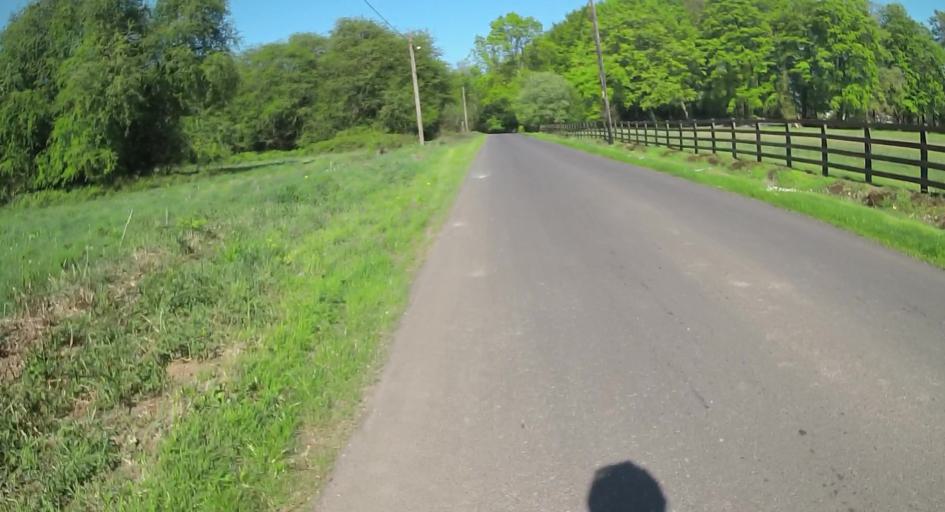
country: GB
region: England
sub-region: Hampshire
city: Alton
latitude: 51.1850
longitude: -1.0017
